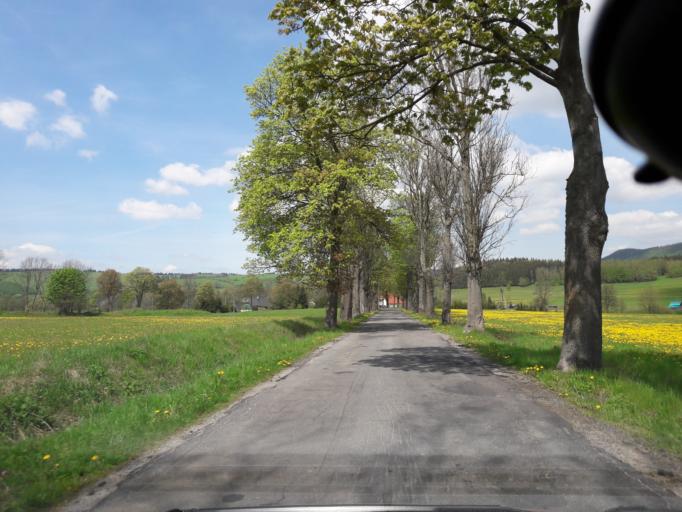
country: PL
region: Lower Silesian Voivodeship
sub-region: Powiat klodzki
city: Duszniki-Zdroj
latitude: 50.4232
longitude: 16.3780
